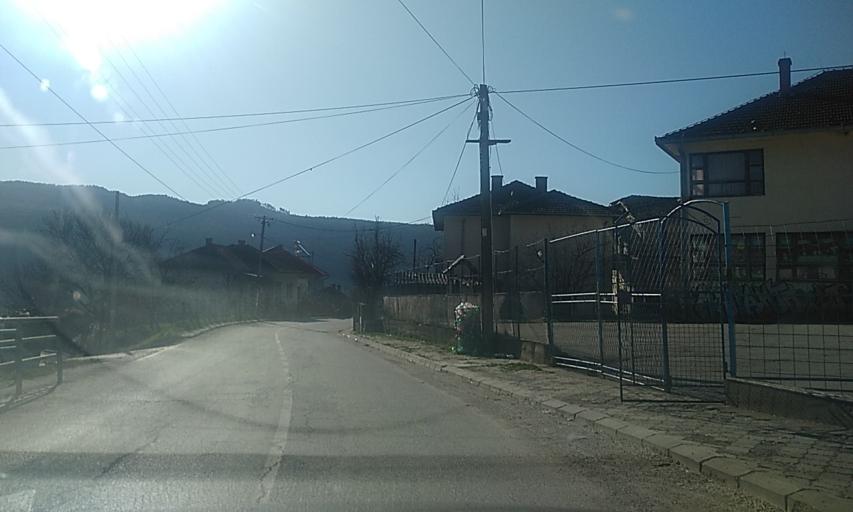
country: RS
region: Central Serbia
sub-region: Pcinjski Okrug
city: Bosilegrad
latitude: 42.4841
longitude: 22.4730
